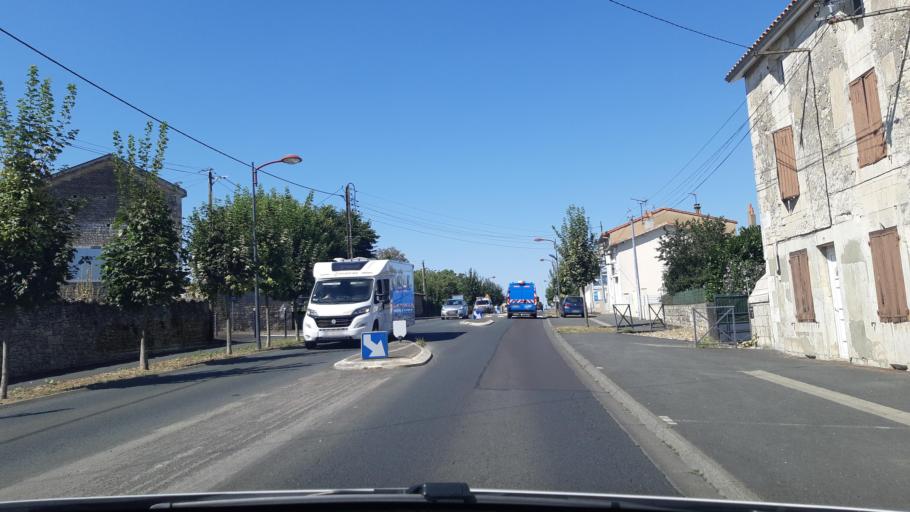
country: FR
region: Poitou-Charentes
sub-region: Departement des Deux-Sevres
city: La Creche
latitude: 46.3567
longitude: -0.3076
